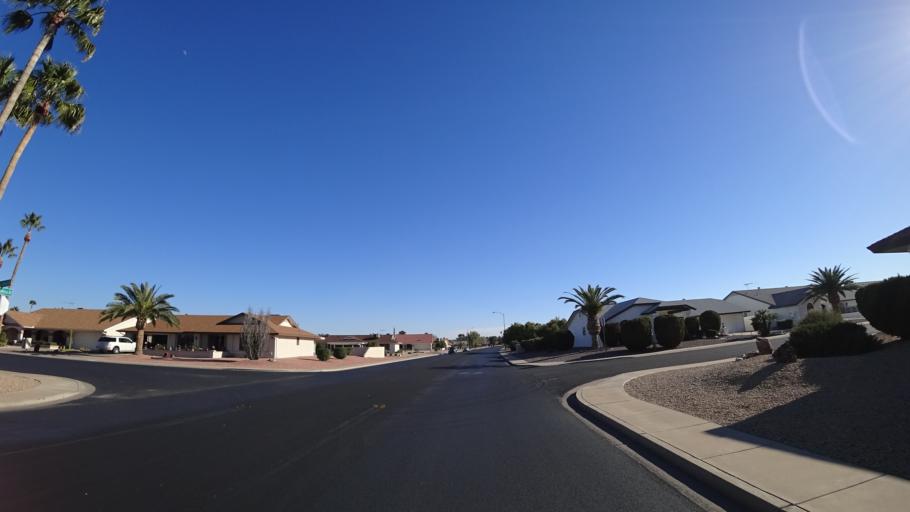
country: US
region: Arizona
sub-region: Maricopa County
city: Sun City West
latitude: 33.6727
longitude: -112.3616
